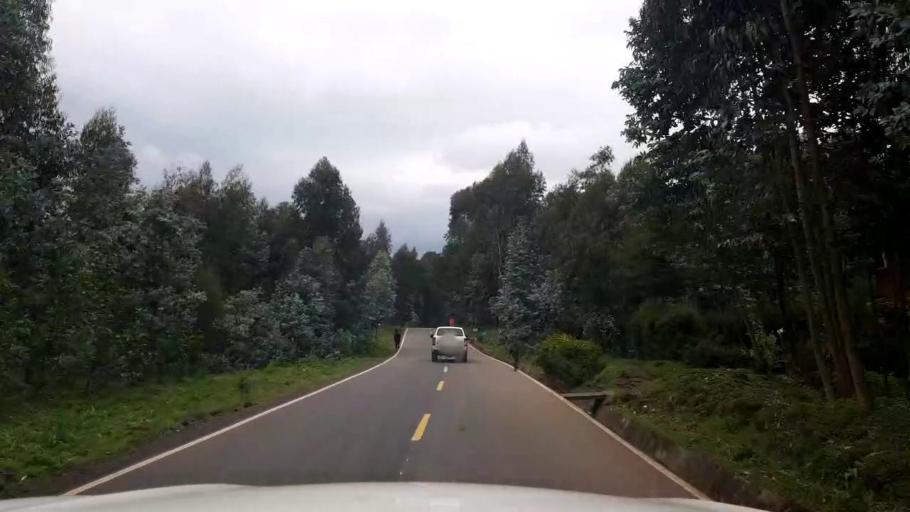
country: RW
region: Northern Province
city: Musanze
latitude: -1.4373
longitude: 29.5491
